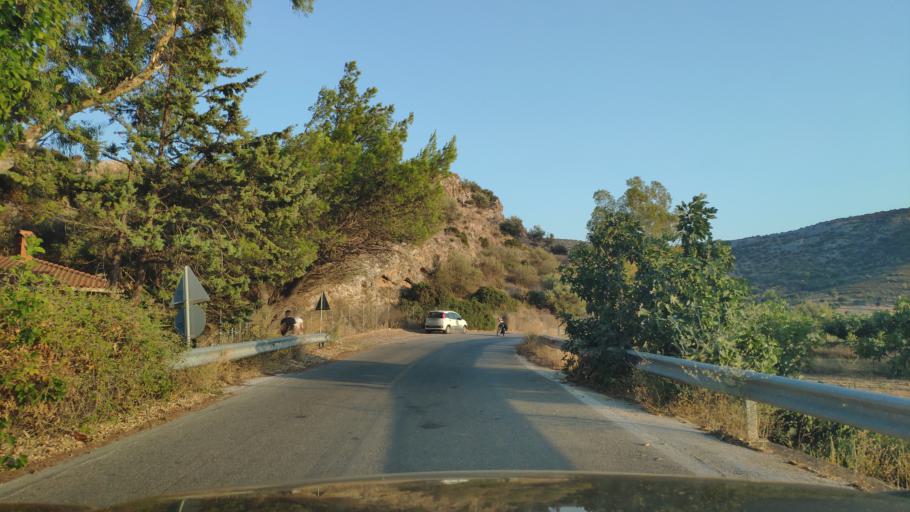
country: GR
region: Attica
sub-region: Nomarchia Anatolikis Attikis
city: Limin Mesoyaias
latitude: 37.9259
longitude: 23.9930
